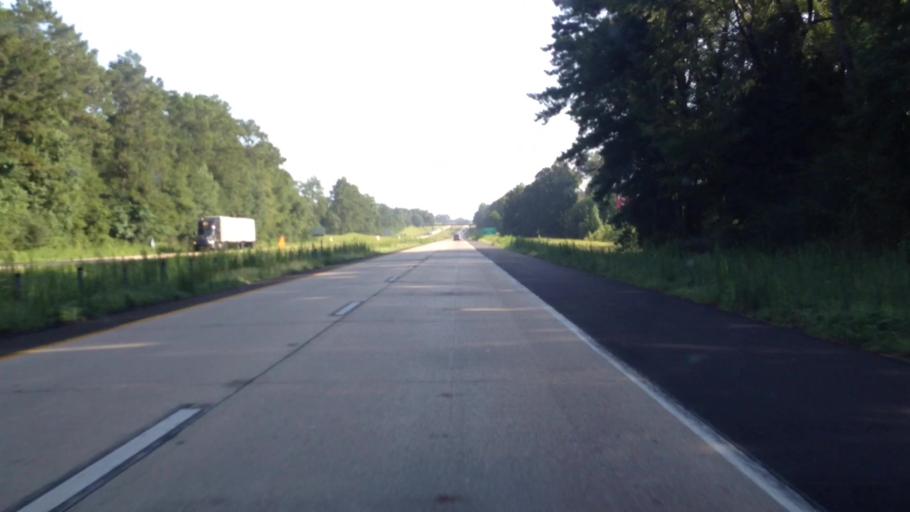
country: US
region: Mississippi
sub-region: Pike County
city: Summit
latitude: 31.2745
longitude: -90.4789
